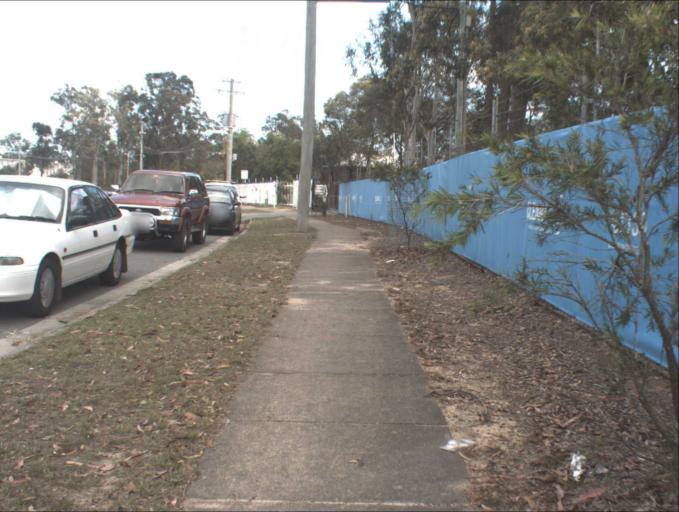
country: AU
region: Queensland
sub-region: Logan
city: Logan Reserve
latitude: -27.6778
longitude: 153.0731
